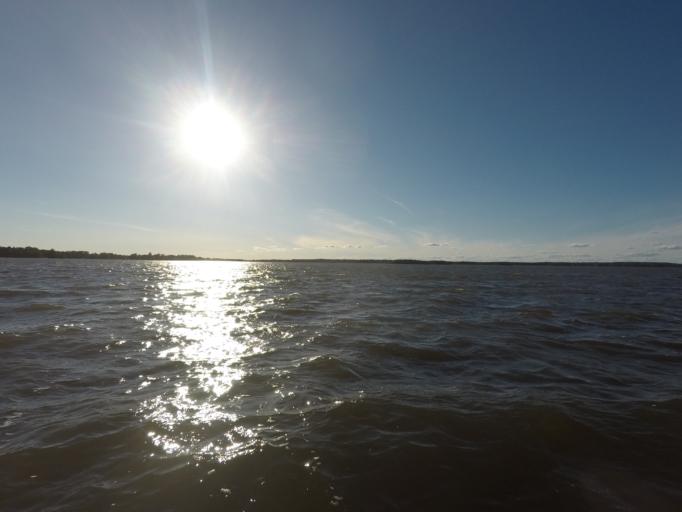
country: SE
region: Vaestmanland
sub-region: Vasteras
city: Vasteras
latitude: 59.5193
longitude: 16.5869
